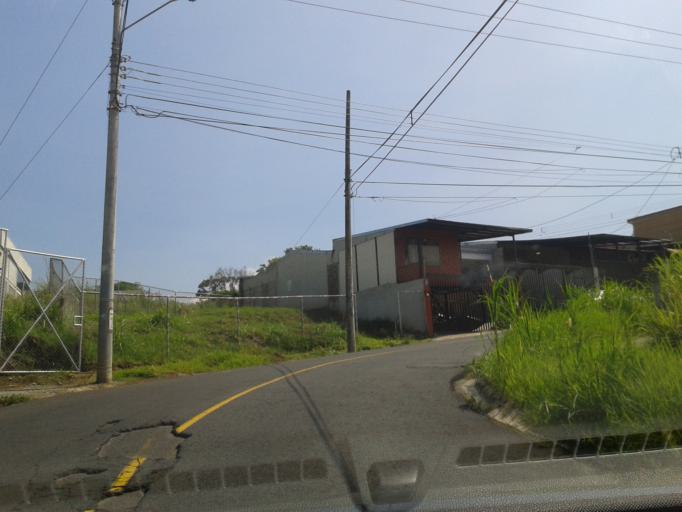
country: CR
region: Heredia
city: San Francisco
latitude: 9.9822
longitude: -84.1380
